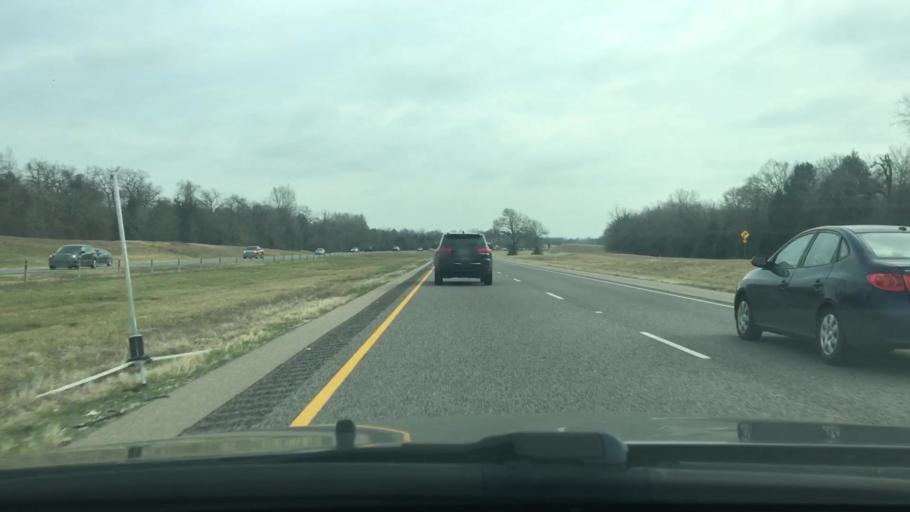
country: US
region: Texas
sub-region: Leon County
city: Buffalo
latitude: 31.5064
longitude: -96.1005
